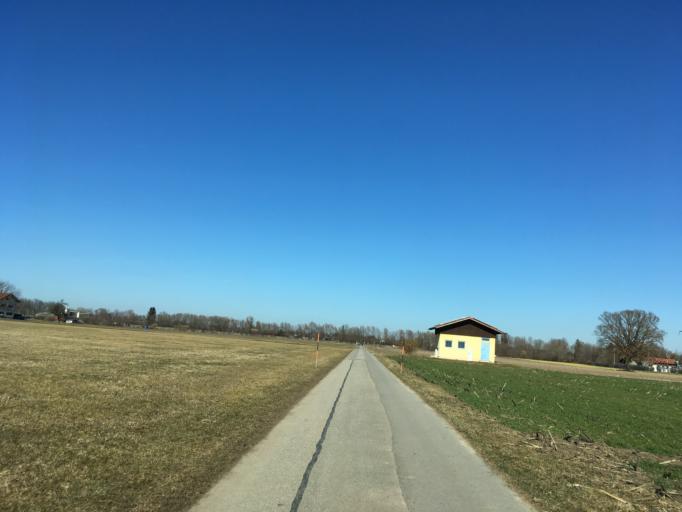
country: DE
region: Bavaria
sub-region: Upper Bavaria
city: Bad Aibling
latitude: 47.8477
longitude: 11.9993
